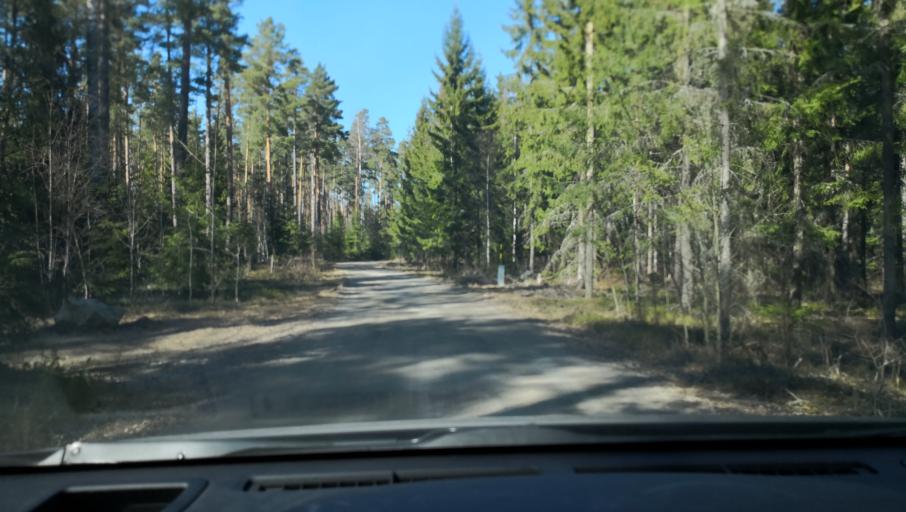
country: SE
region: Vaestmanland
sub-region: Sala Kommun
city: Sala
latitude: 59.9371
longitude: 16.4523
